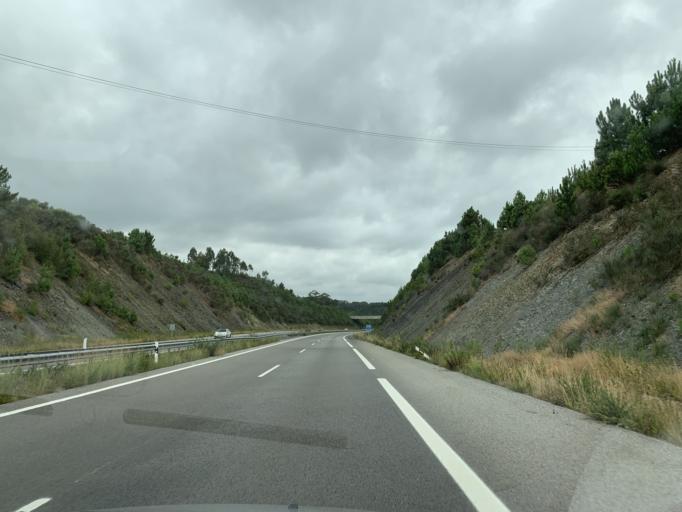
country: ES
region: Asturias
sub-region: Province of Asturias
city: El Franco
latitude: 43.5476
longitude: -6.8677
